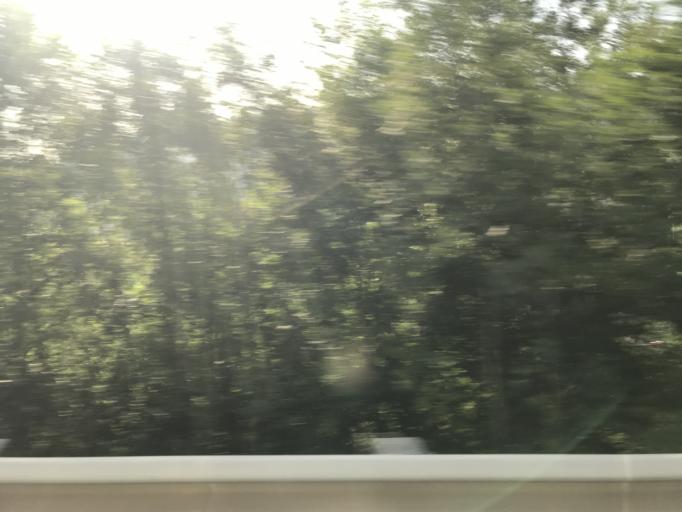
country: ES
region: Basque Country
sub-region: Provincia de Guipuzcoa
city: Idiazabal
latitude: 43.0106
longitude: -2.2361
